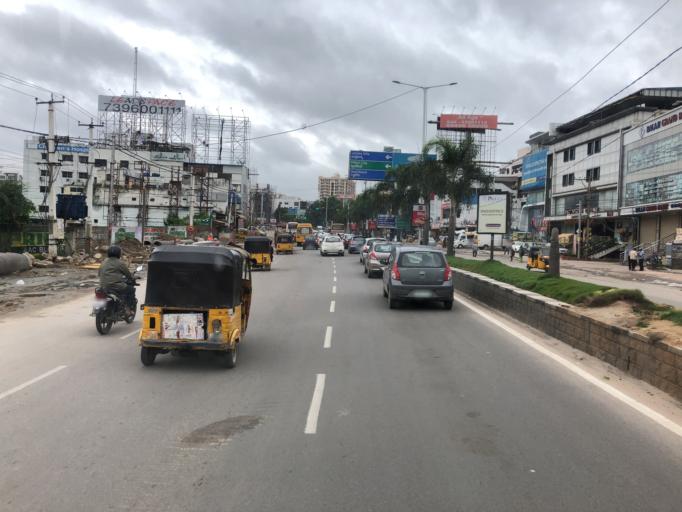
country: IN
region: Telangana
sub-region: Rangareddi
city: Kukatpalli
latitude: 17.4606
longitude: 78.3667
